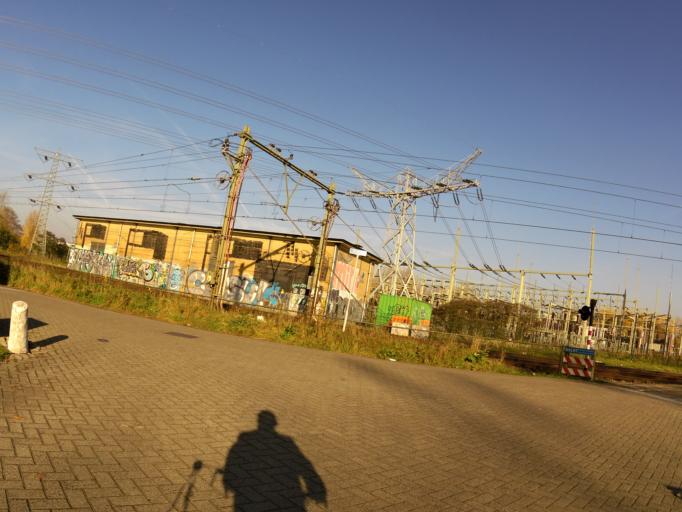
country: NL
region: North Brabant
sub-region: Gemeente 's-Hertogenbosch
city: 's-Hertogenbosch
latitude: 51.7089
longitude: 5.2965
